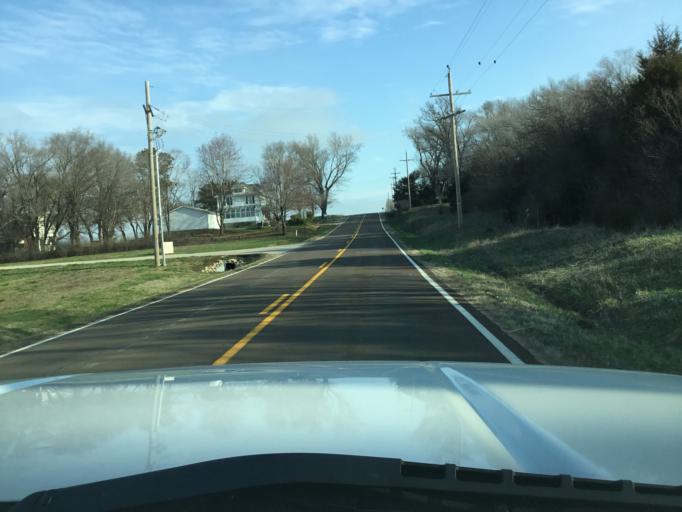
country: US
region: Kansas
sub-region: Shawnee County
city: Topeka
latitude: 39.1041
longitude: -95.7484
